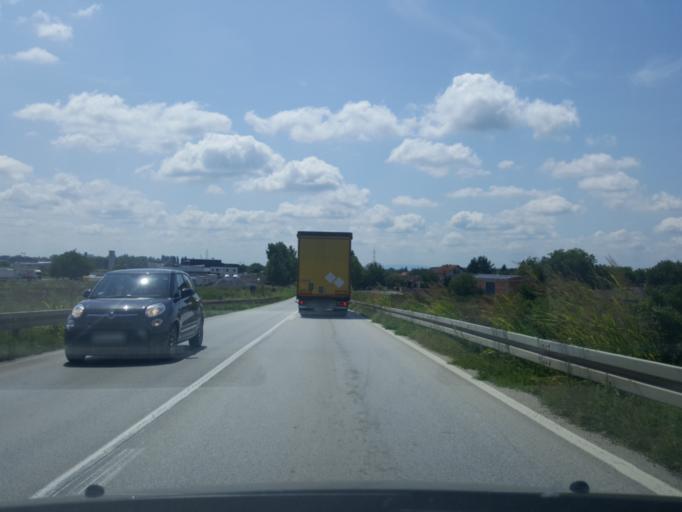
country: RS
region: Autonomna Pokrajina Vojvodina
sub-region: Sremski Okrug
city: Sremska Mitrovica
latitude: 44.9832
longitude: 19.6393
